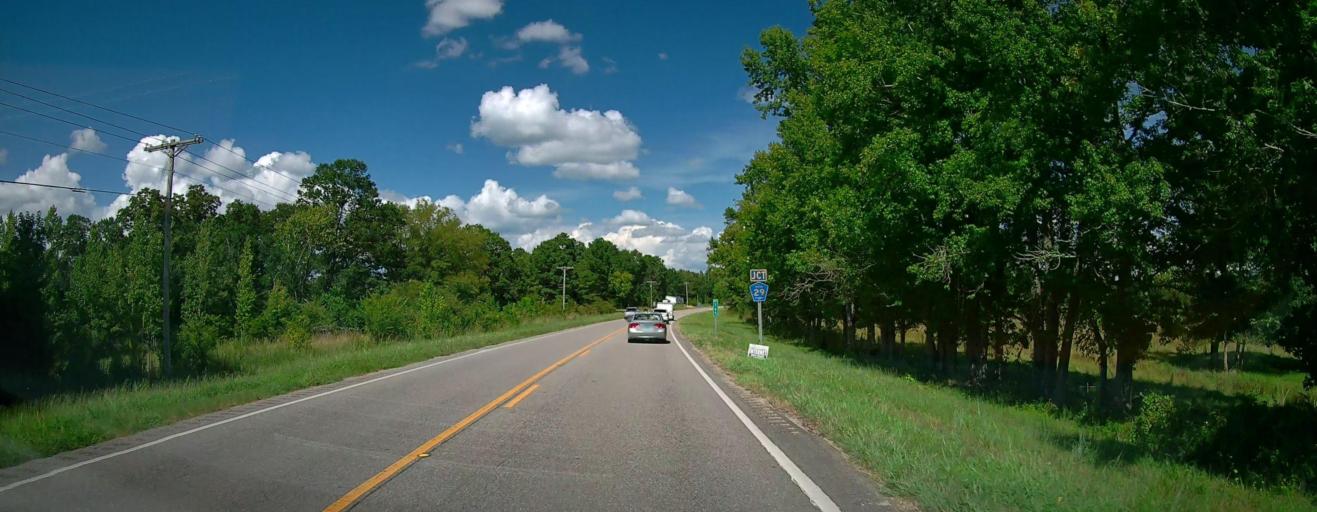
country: US
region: Alabama
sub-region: Macon County
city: Tuskegee
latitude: 32.3827
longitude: -85.8243
